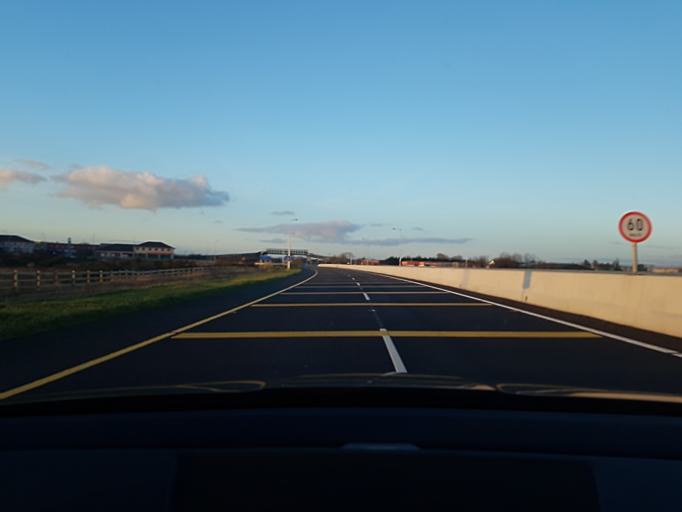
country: IE
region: Connaught
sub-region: County Galway
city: Tuam
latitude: 53.5049
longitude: -8.8779
